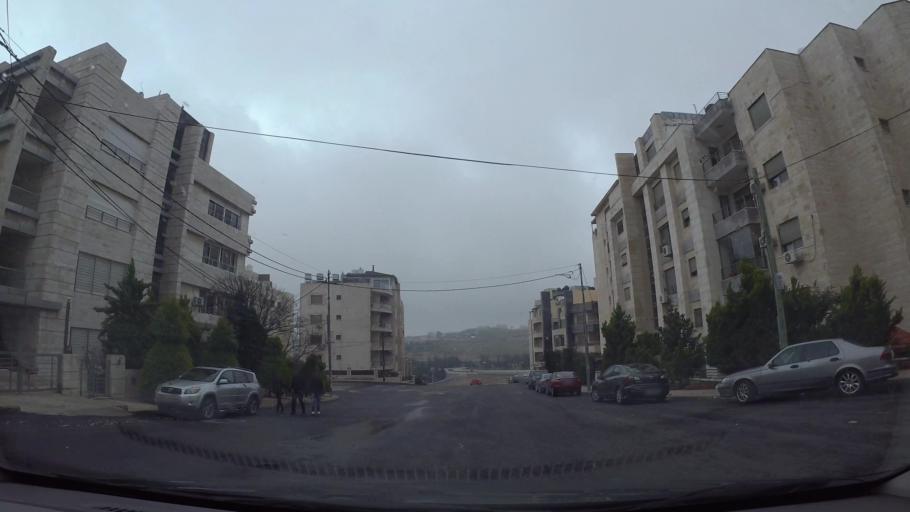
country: JO
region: Amman
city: Wadi as Sir
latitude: 31.9383
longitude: 35.8564
